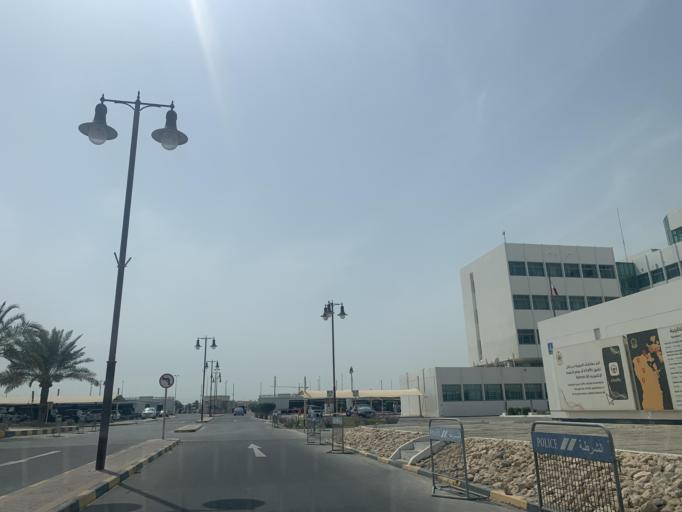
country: BH
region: Northern
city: Madinat `Isa
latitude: 26.1560
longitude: 50.5389
